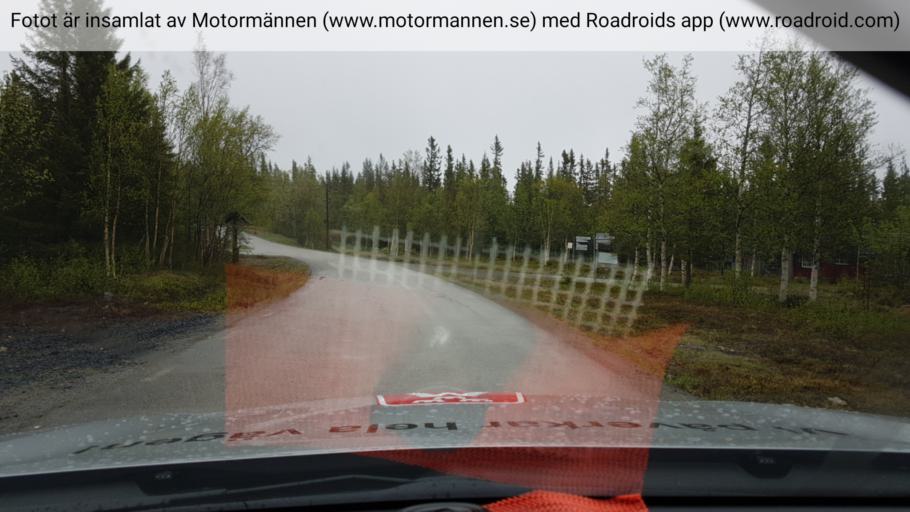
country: SE
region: Jaemtland
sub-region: Bergs Kommun
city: Hoverberg
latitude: 63.0043
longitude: 13.9453
